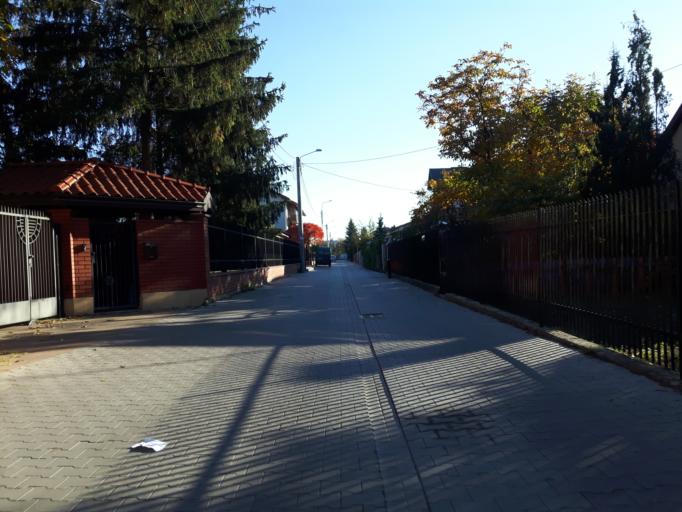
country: PL
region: Masovian Voivodeship
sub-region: Powiat wolominski
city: Zabki
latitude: 52.2872
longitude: 21.1311
